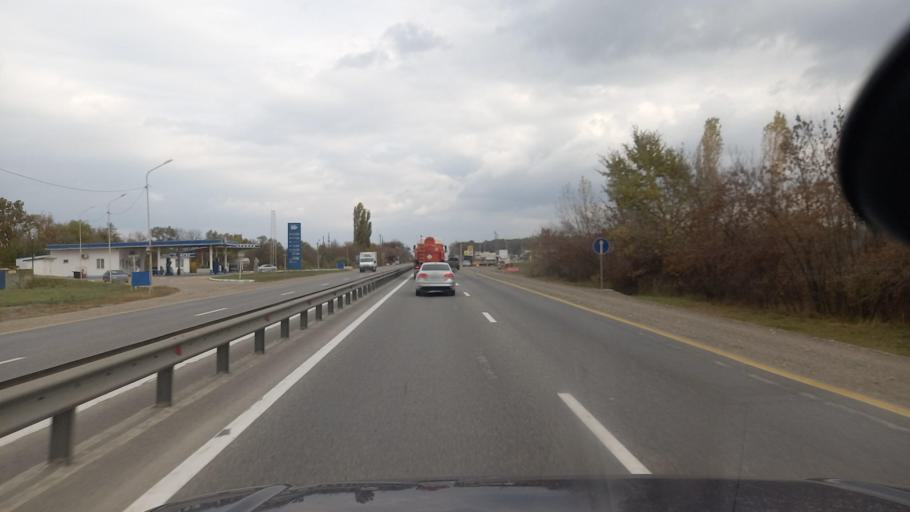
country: RU
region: Krasnodarskiy
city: Afipskiy
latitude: 44.9005
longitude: 38.8697
